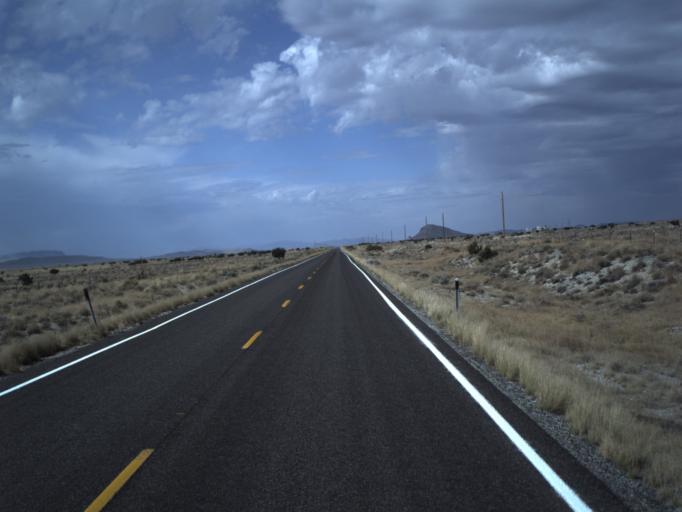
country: US
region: Utah
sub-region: Tooele County
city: Wendover
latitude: 41.4385
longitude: -113.7270
